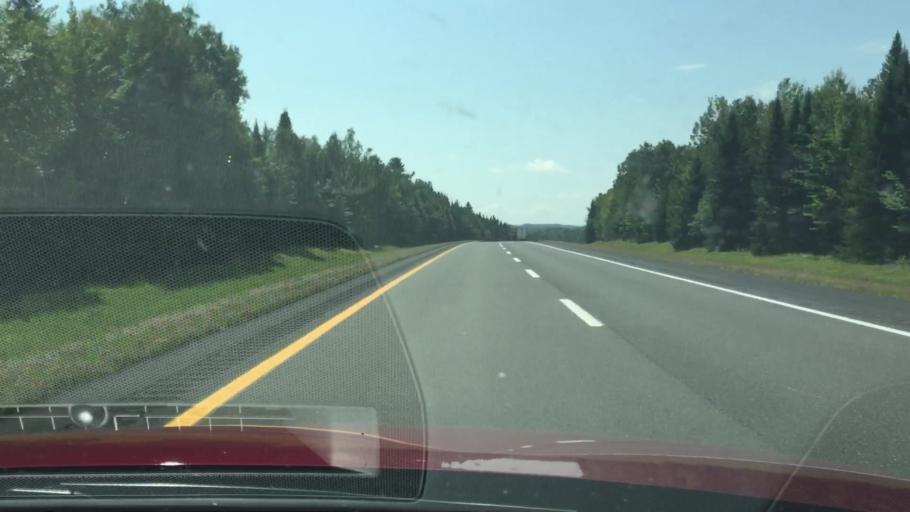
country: US
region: Maine
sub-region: Penobscot County
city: Patten
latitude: 45.9728
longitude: -68.2972
